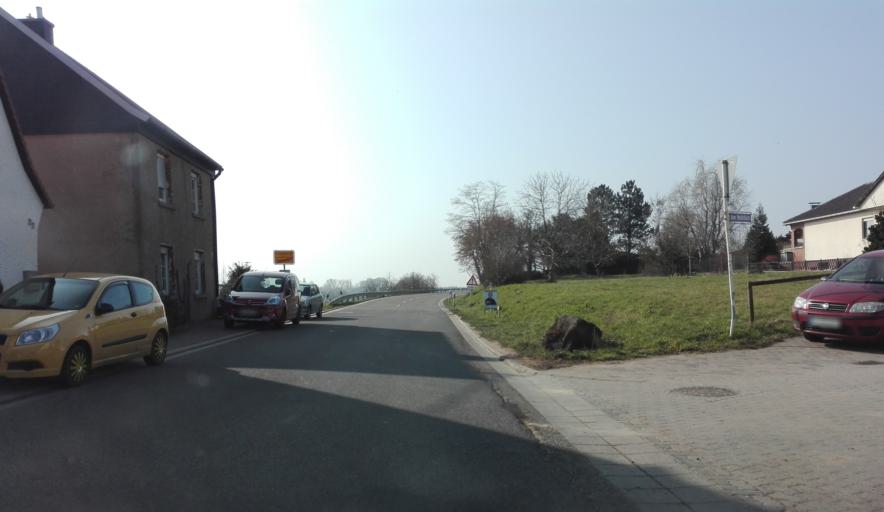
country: DE
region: Rheinland-Pfalz
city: Kleinniedesheim
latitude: 49.5860
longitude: 8.3213
